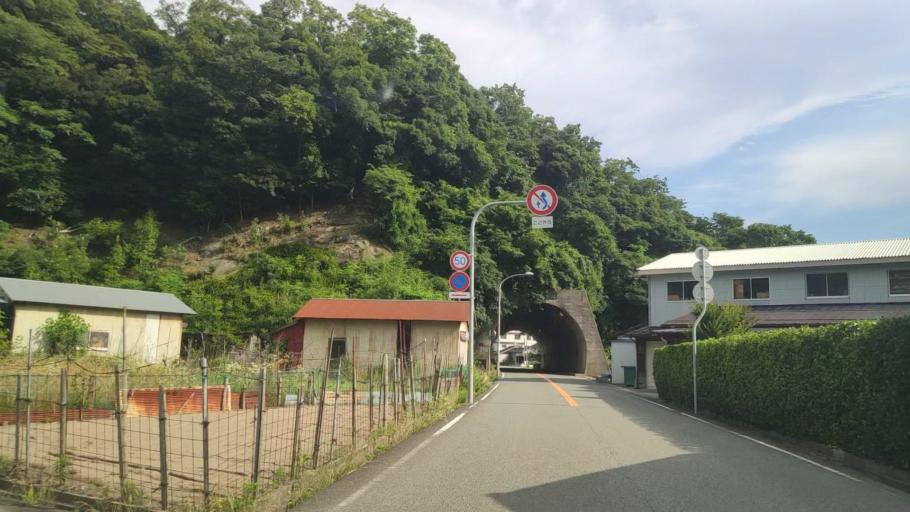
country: JP
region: Hyogo
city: Toyooka
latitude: 35.6390
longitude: 134.8361
